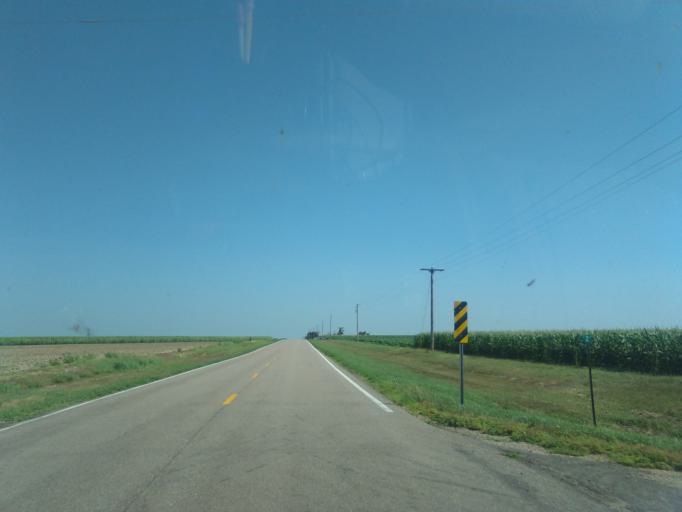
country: US
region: Kansas
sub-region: Cheyenne County
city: Saint Francis
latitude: 39.7859
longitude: -101.5419
